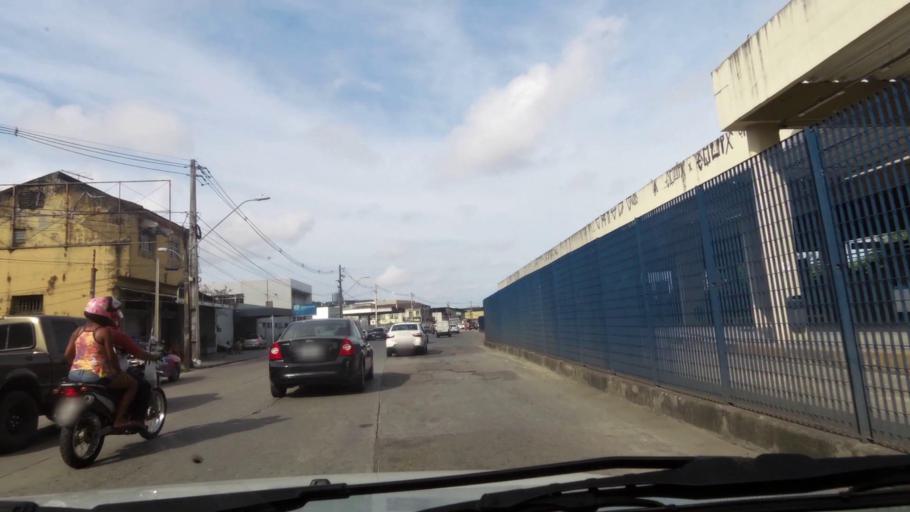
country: BR
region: Pernambuco
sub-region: Recife
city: Recife
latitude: -8.0800
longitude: -34.9037
